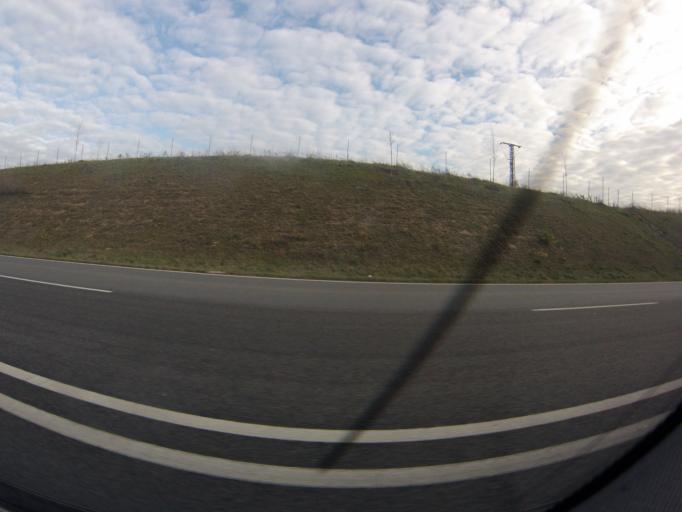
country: DE
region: Thuringia
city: Gossnitz
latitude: 50.8866
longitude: 12.4409
